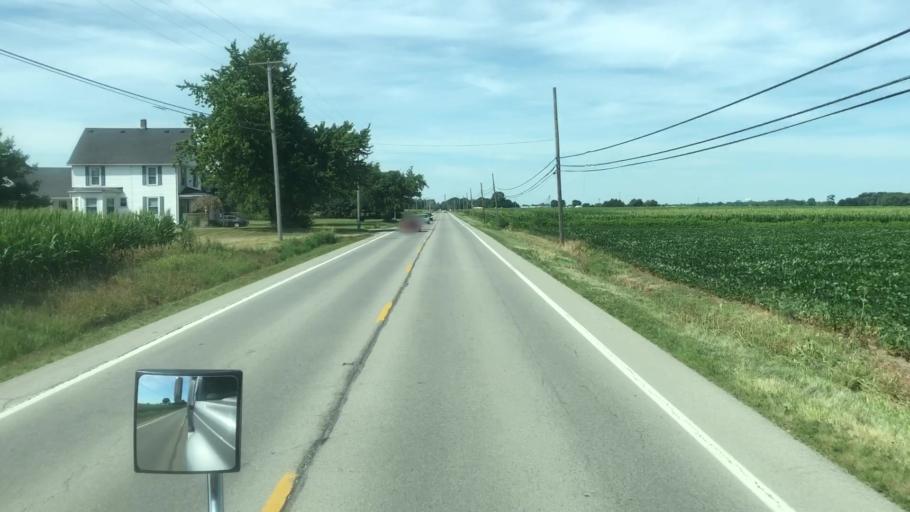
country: US
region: Ohio
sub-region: Sandusky County
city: Fremont
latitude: 41.3759
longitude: -83.0628
